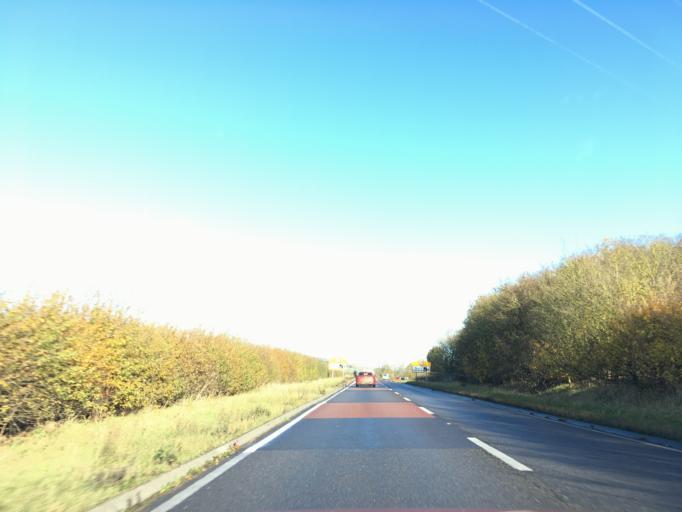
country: GB
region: England
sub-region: Gloucestershire
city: Gotherington
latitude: 52.0093
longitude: -2.0463
